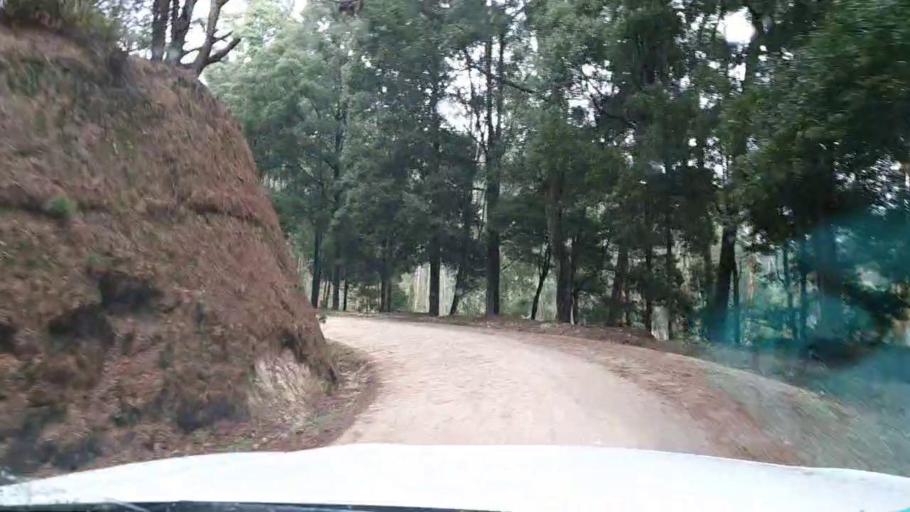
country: RW
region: Southern Province
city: Nzega
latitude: -2.3651
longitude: 29.3779
